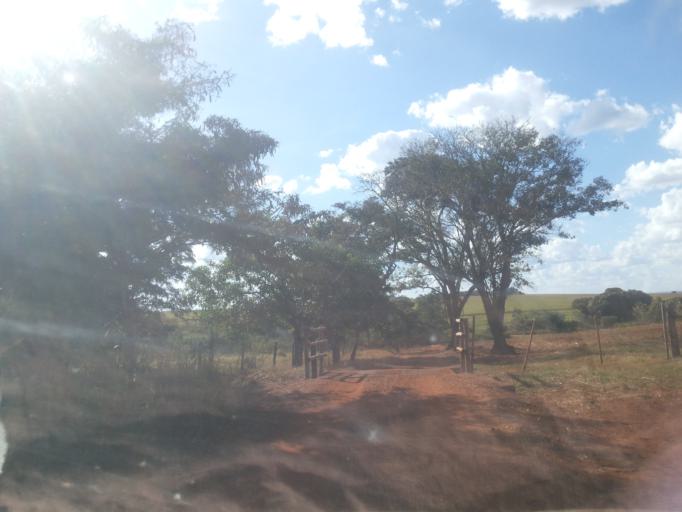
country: BR
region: Minas Gerais
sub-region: Capinopolis
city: Capinopolis
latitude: -18.5862
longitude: -49.4952
